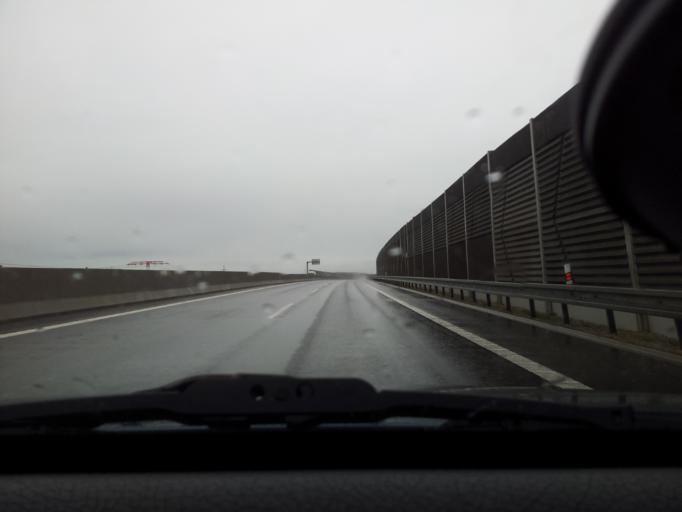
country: SK
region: Nitriansky
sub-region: Okres Nitra
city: Nitra
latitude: 48.2888
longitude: 18.0493
